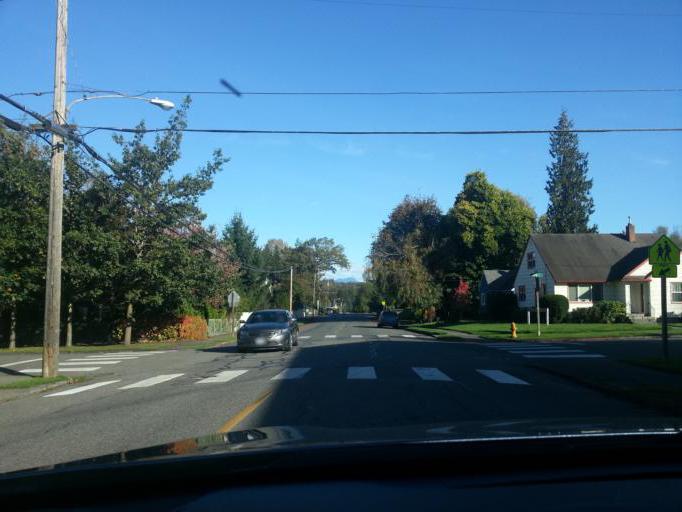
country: US
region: Washington
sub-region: Snohomish County
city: Snohomish
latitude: 47.9159
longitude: -122.0932
